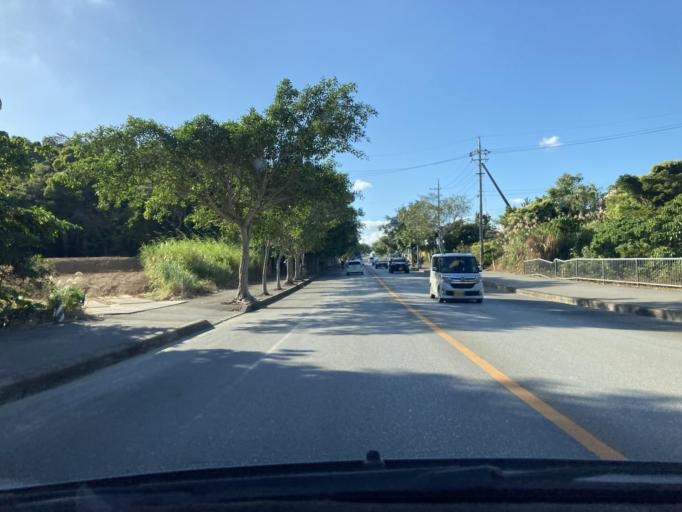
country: JP
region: Okinawa
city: Gushikawa
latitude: 26.3684
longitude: 127.8372
